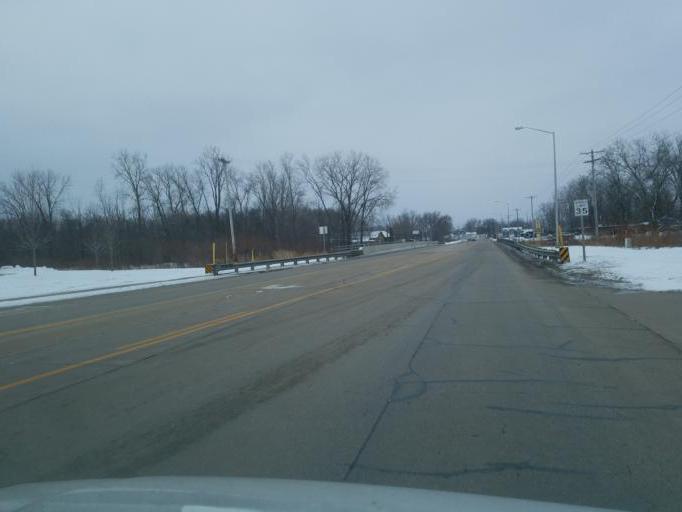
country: US
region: Wisconsin
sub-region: Waupaca County
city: New London
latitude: 44.4015
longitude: -88.7438
